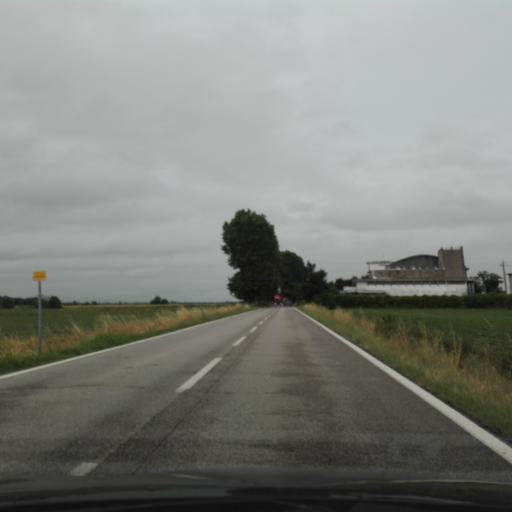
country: IT
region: Veneto
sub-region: Provincia di Padova
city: Barbona
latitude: 45.0783
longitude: 11.7183
